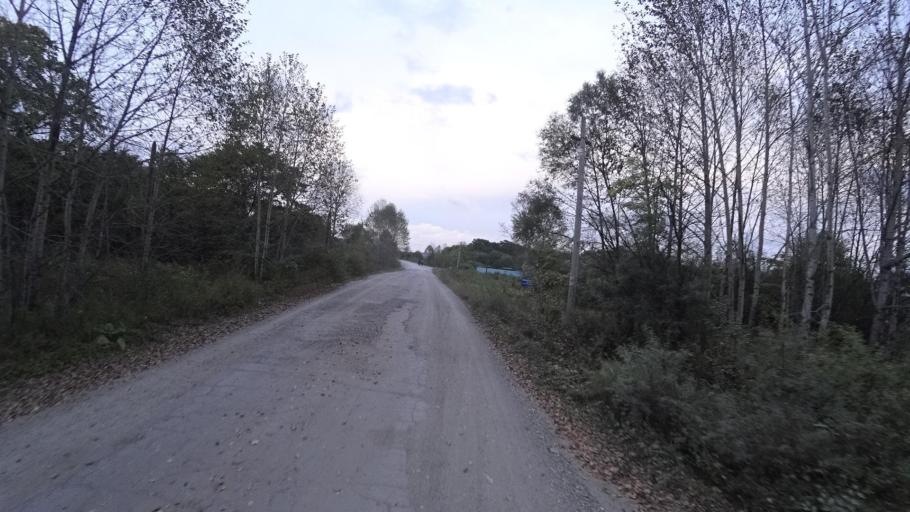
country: RU
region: Jewish Autonomous Oblast
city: Izvestkovyy
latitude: 48.9898
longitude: 131.5539
